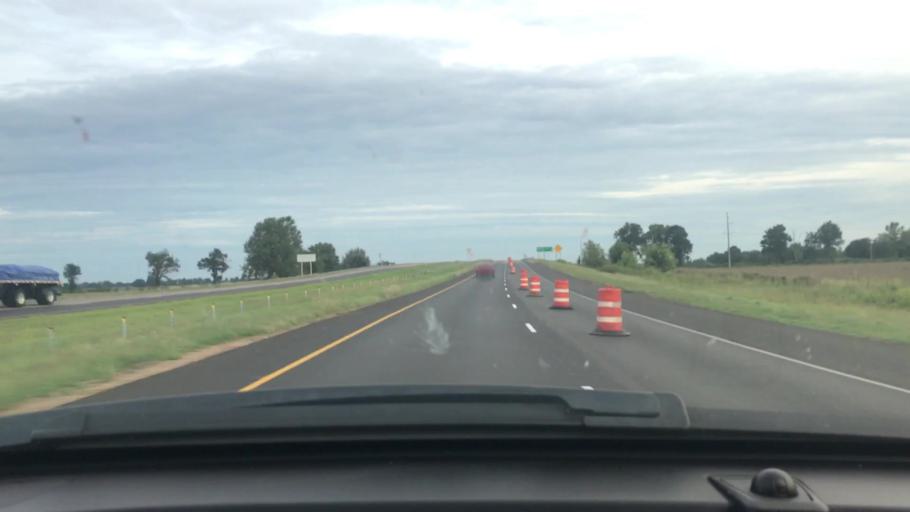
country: US
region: Arkansas
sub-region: Poinsett County
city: Trumann
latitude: 35.6238
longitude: -90.4968
